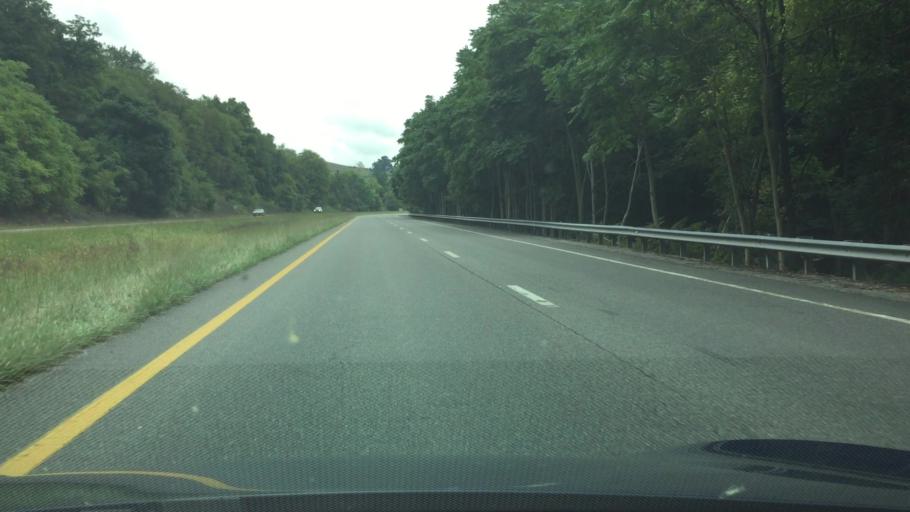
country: US
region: Virginia
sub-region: City of Radford
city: Radford
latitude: 37.1114
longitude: -80.5240
